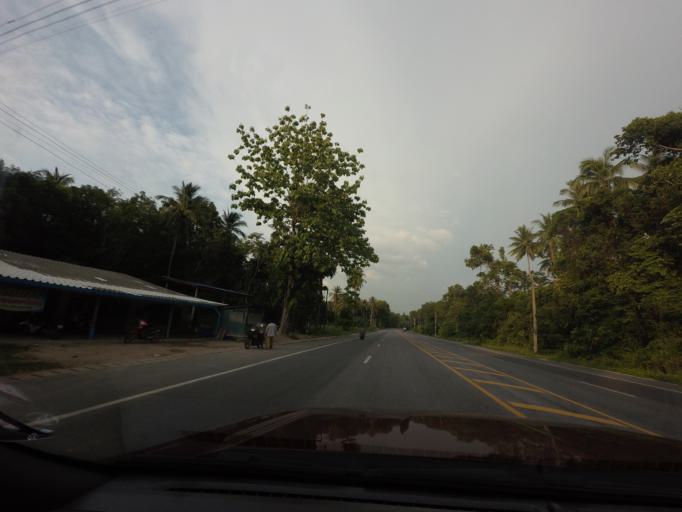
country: TH
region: Pattani
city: Khok Pho
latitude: 6.6765
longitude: 101.1322
